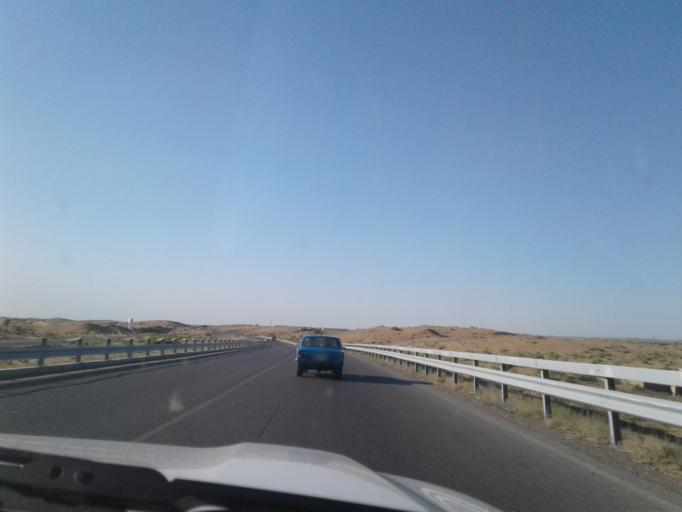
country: TM
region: Mary
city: Yoloeten
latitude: 37.1134
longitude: 62.4430
